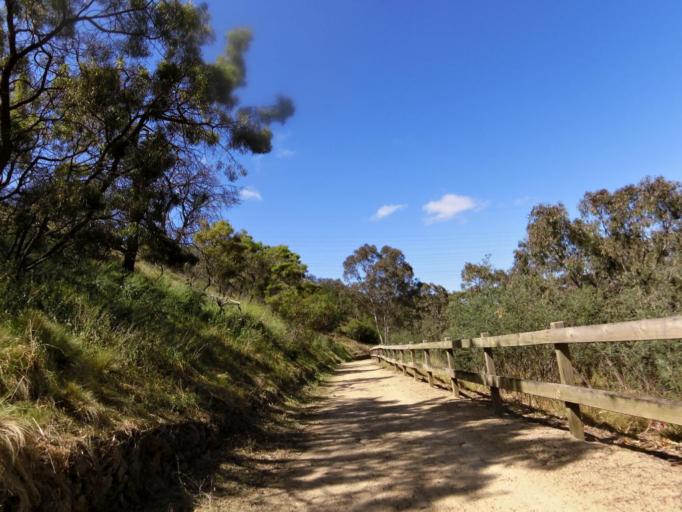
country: AU
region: Victoria
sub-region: Brimbank
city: Kealba
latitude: -37.7419
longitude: 144.8380
